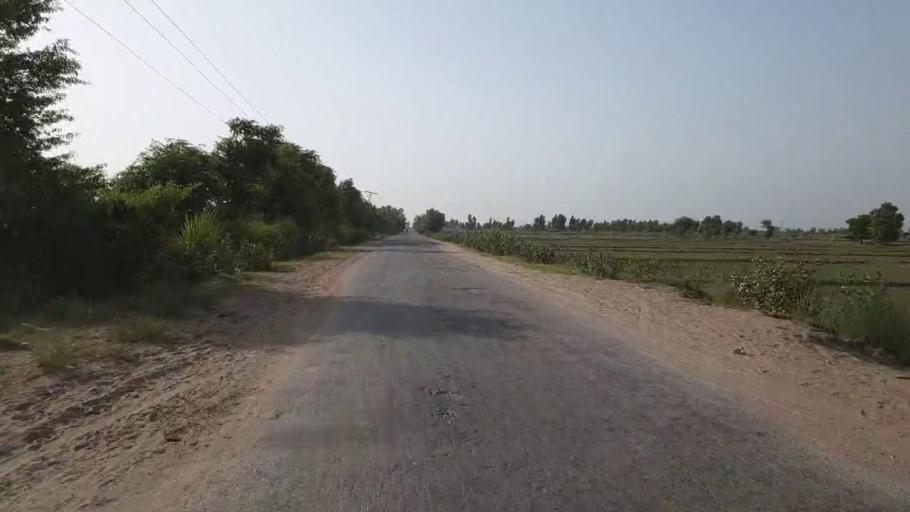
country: PK
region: Sindh
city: Jam Sahib
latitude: 26.3869
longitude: 68.8829
